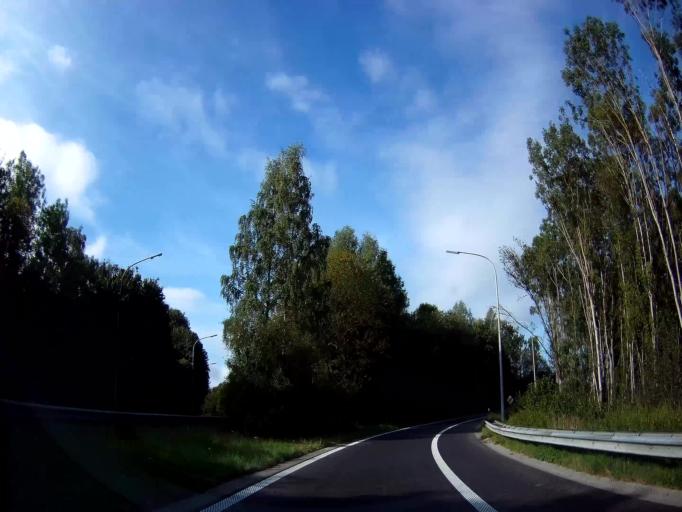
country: BE
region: Wallonia
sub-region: Province de Namur
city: Ciney
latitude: 50.2671
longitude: 5.0393
